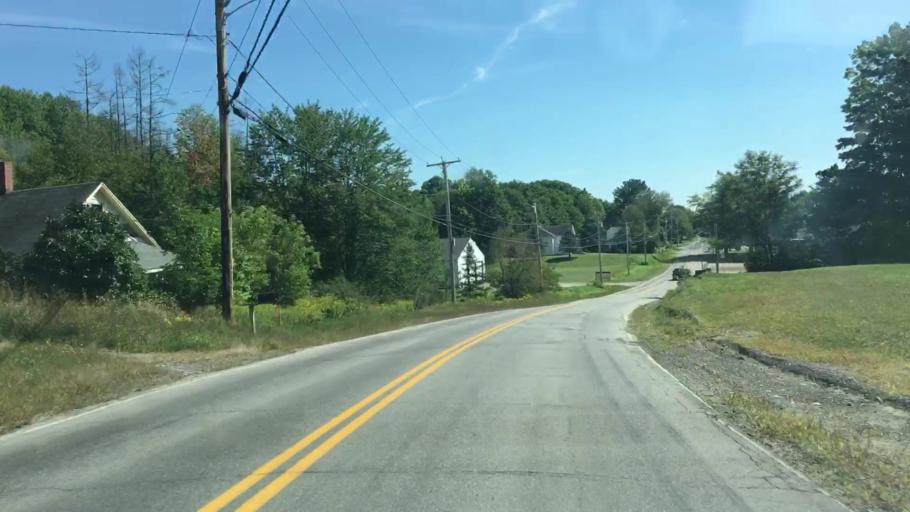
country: US
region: Maine
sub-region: Penobscot County
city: Bradford
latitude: 45.1692
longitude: -68.8471
